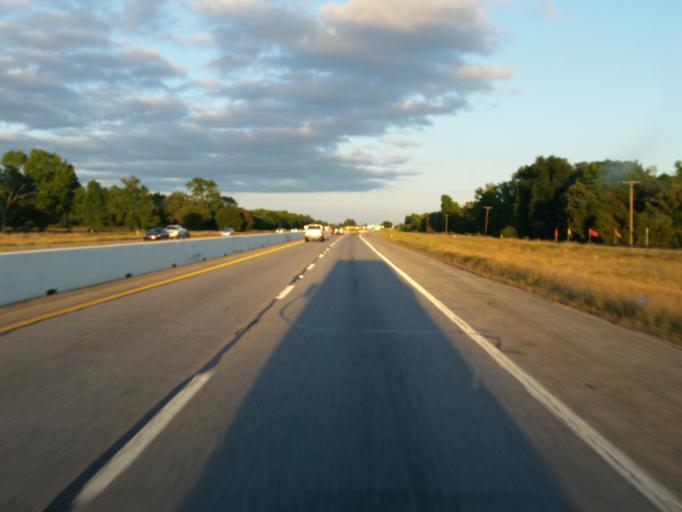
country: US
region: Texas
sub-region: Van Zandt County
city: Van
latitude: 32.5323
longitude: -95.7290
